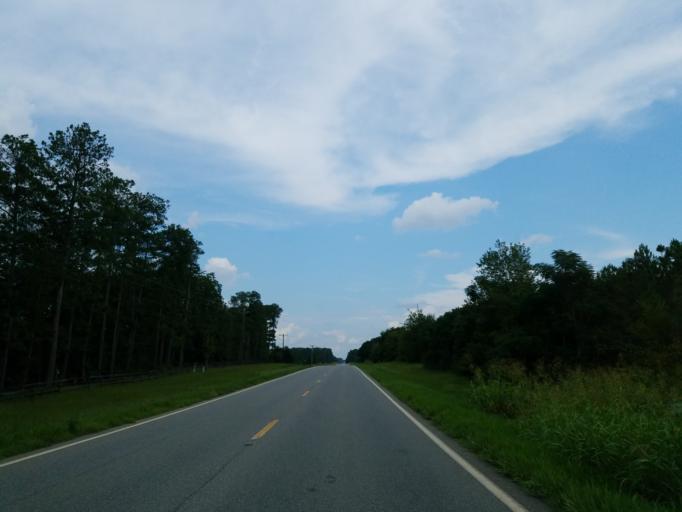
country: US
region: Georgia
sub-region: Dooly County
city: Unadilla
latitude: 32.3309
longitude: -83.7467
